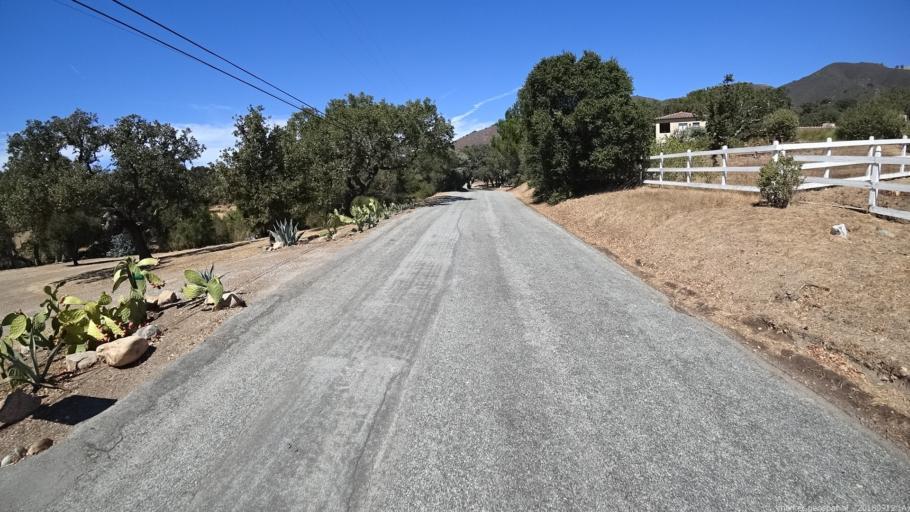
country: US
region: California
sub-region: Monterey County
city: Carmel Valley Village
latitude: 36.4970
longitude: -121.7469
